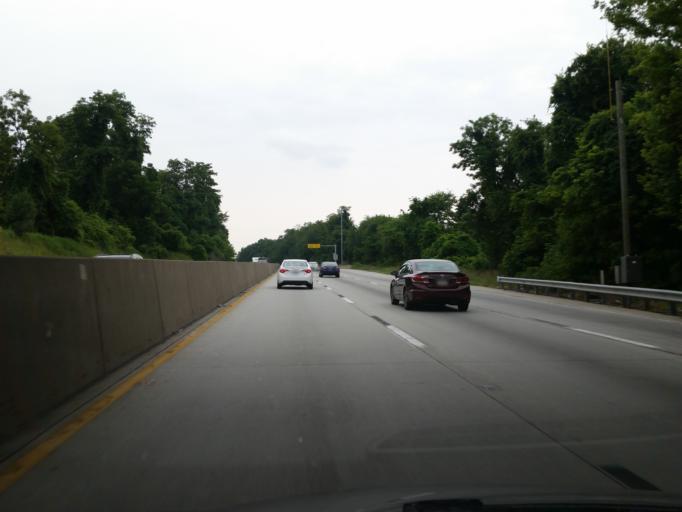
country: US
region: Pennsylvania
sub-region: Dauphin County
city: Steelton
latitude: 40.1904
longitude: -76.8480
